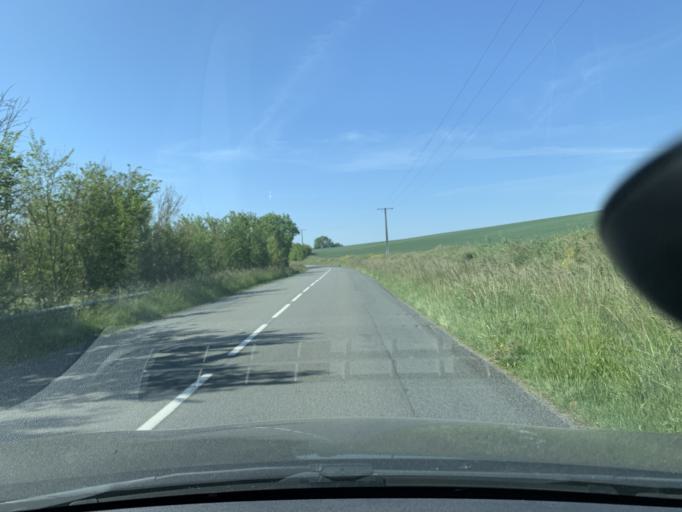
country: FR
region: Nord-Pas-de-Calais
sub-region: Departement du Nord
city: Masnieres
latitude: 50.0839
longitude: 3.2184
